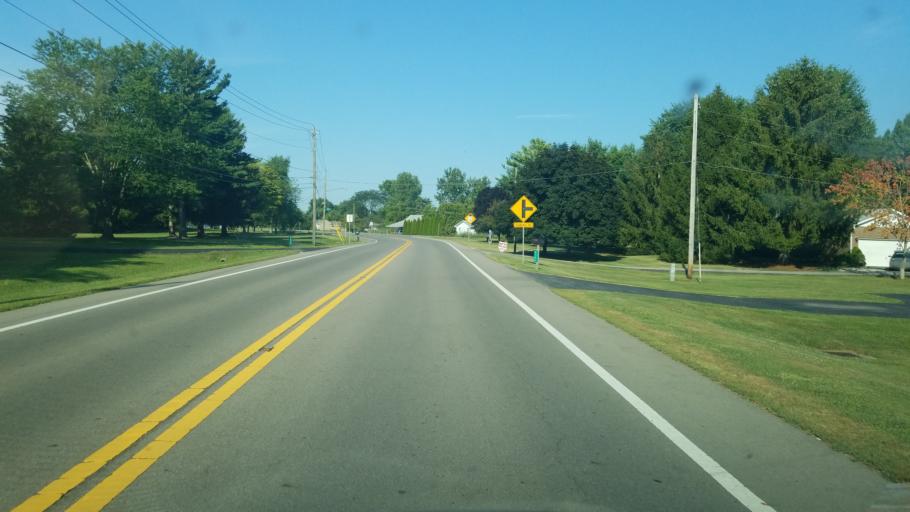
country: US
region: Ohio
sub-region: Franklin County
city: Grove City
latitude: 39.8601
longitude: -83.1740
